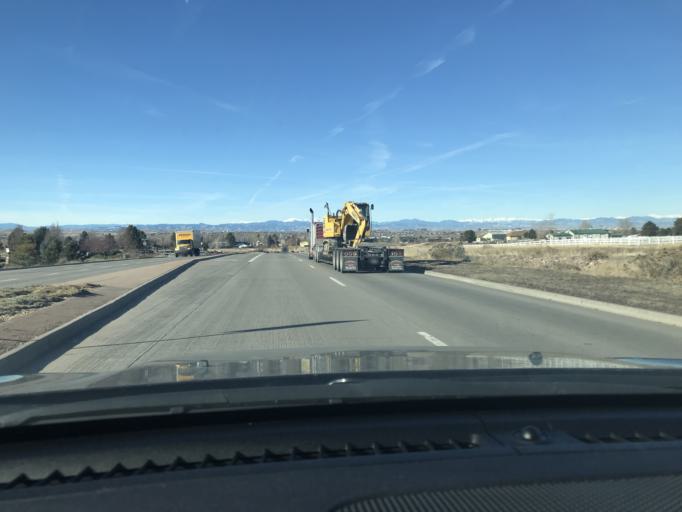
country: US
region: Colorado
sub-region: Douglas County
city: Parker
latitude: 39.5365
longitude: -104.7570
